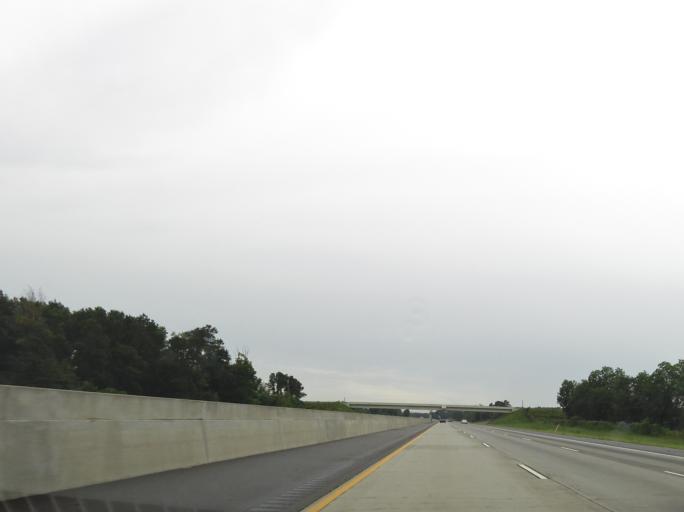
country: US
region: Georgia
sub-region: Tift County
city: Omega
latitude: 31.2964
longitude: -83.4773
